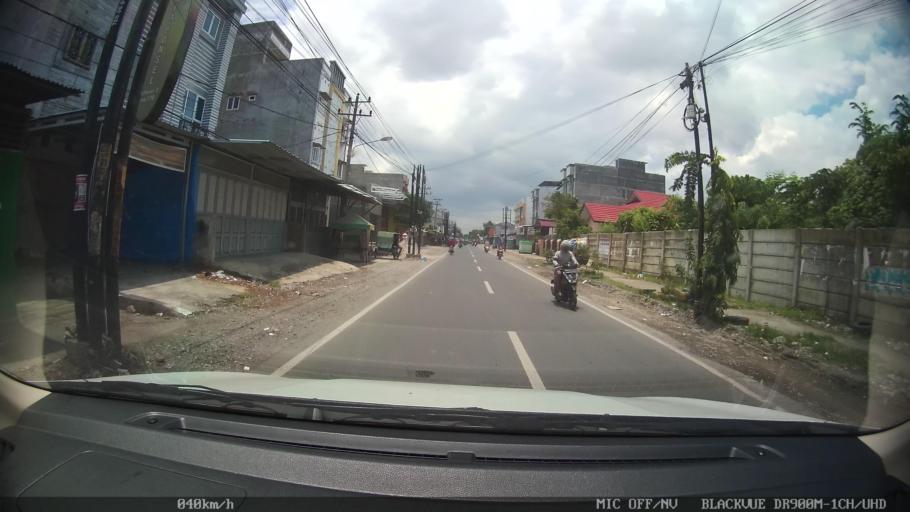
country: ID
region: North Sumatra
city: Medan
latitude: 3.6162
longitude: 98.6928
